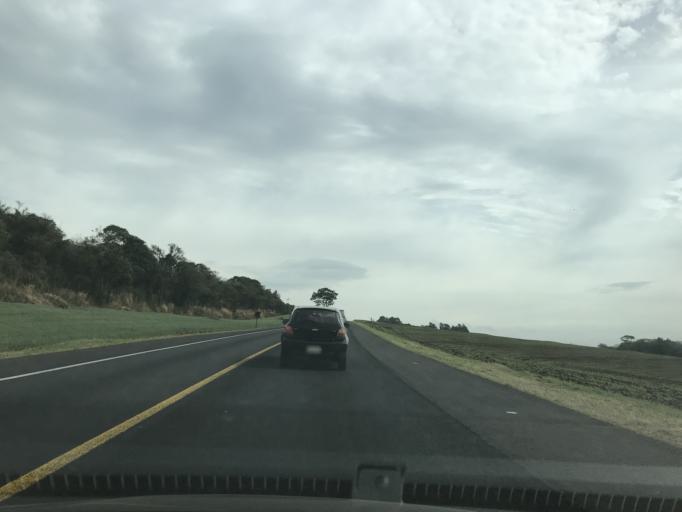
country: BR
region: Parana
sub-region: Matelandia
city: Matelandia
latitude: -25.1077
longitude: -53.7487
